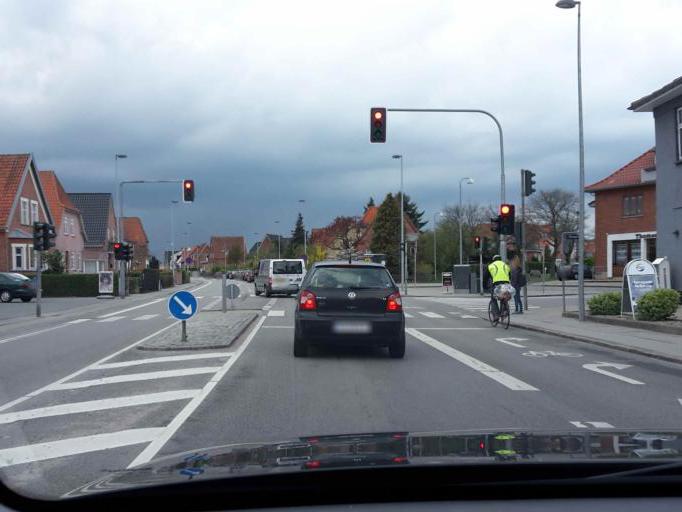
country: DK
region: South Denmark
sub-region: Odense Kommune
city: Odense
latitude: 55.4069
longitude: 10.3503
